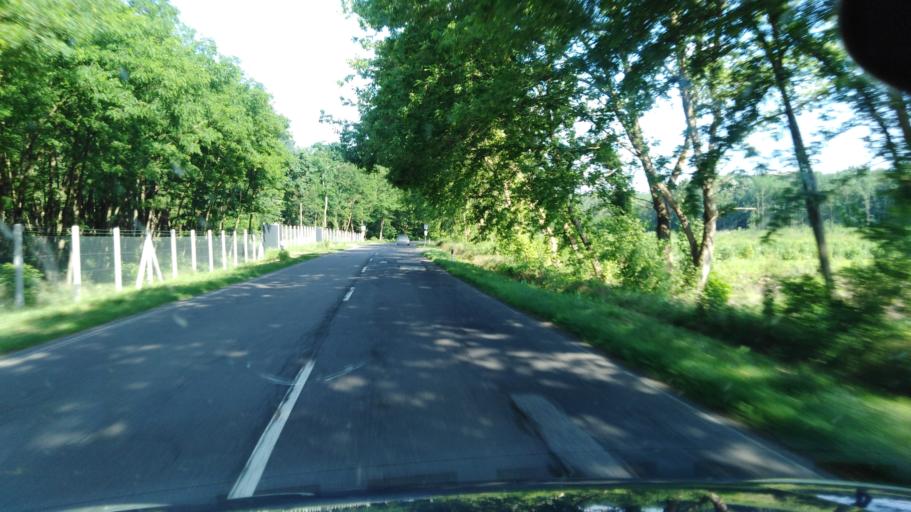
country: HU
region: Szabolcs-Szatmar-Bereg
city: Nyirvasvari
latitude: 47.8103
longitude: 22.2318
